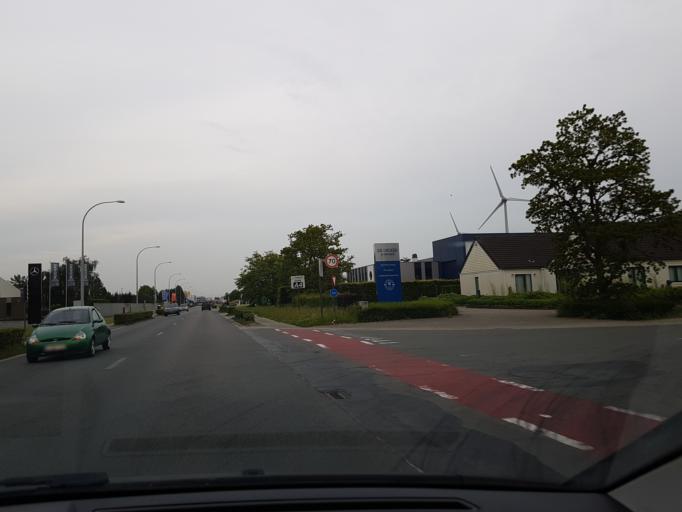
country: BE
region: Flanders
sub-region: Provincie Oost-Vlaanderen
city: Lebbeke
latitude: 51.0318
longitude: 4.1368
